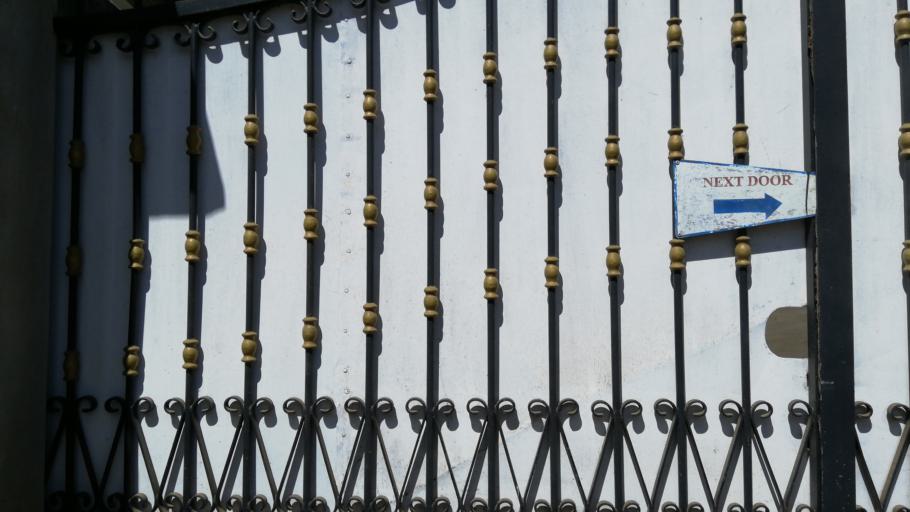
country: MU
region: Moka
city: Moka
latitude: -20.2247
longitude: 57.4733
